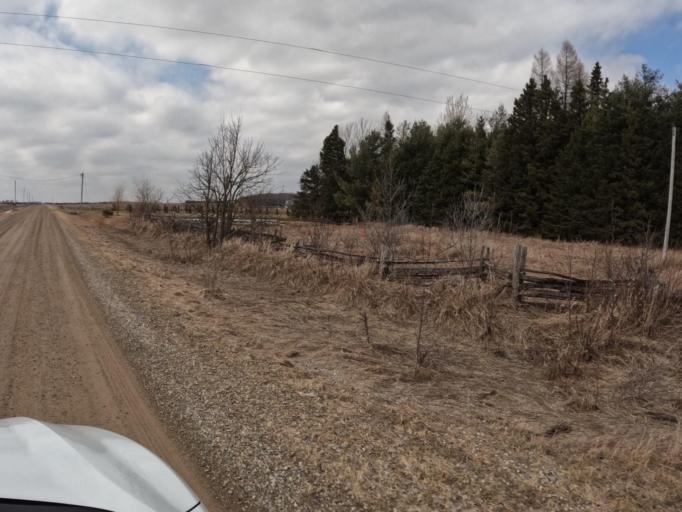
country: CA
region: Ontario
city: Shelburne
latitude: 44.0493
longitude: -80.2968
